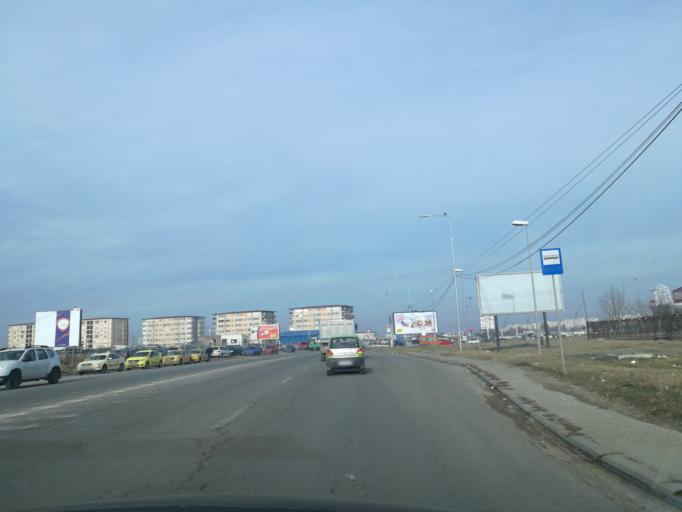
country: RO
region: Constanta
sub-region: Municipiul Constanta
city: Palazu Mare
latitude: 44.1975
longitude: 28.6052
